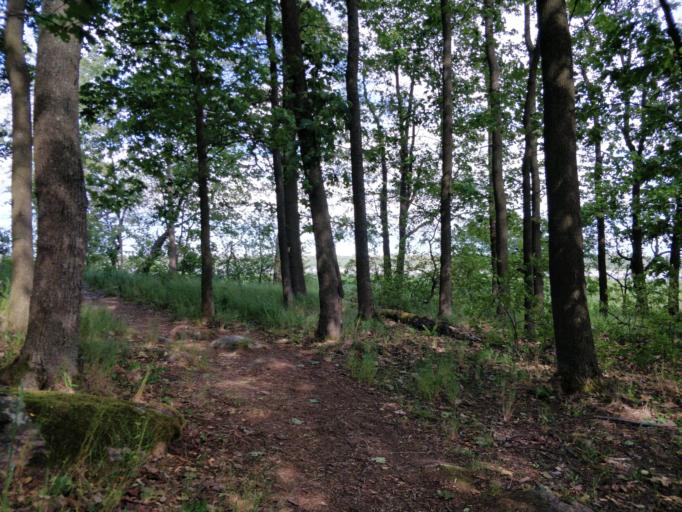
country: FI
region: Uusimaa
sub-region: Helsinki
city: Helsinki
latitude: 60.2028
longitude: 24.9954
